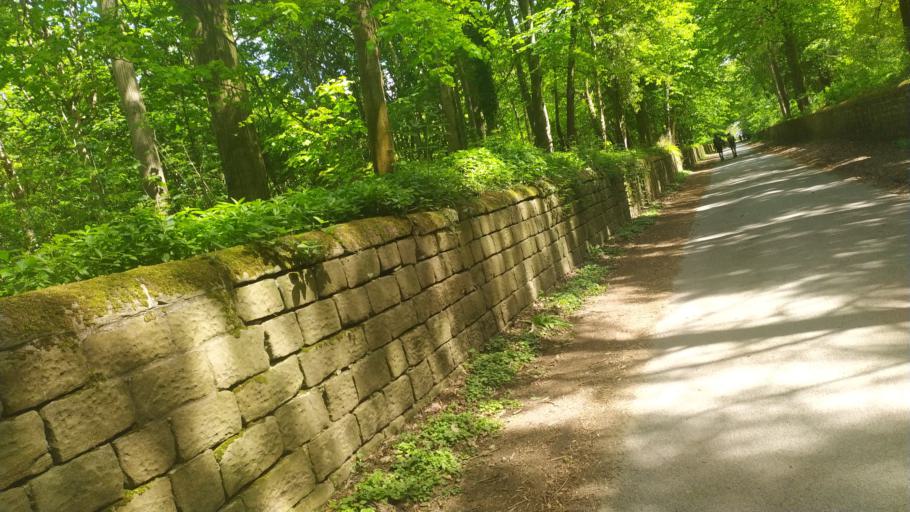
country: GB
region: England
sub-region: North Yorkshire
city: Pannal
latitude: 53.9022
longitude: -1.5186
